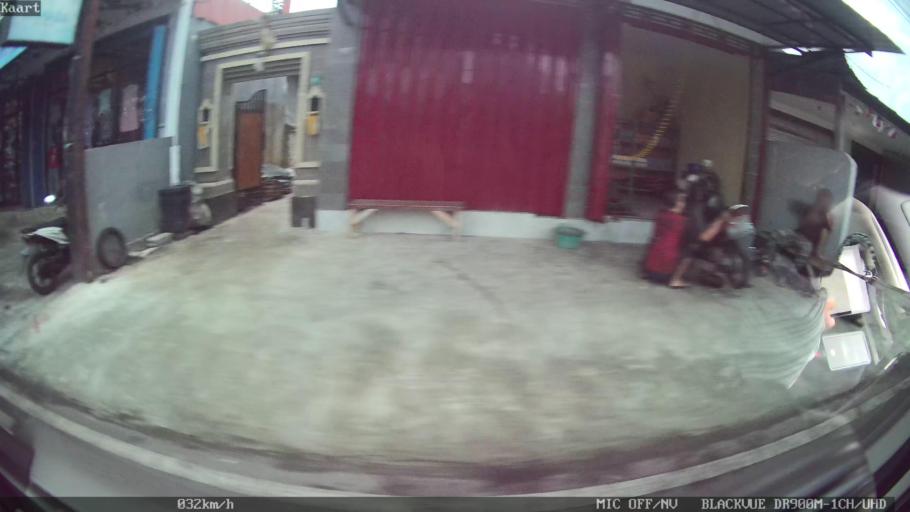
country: ID
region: Bali
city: Banjar Bucu
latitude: -8.5870
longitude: 115.2075
